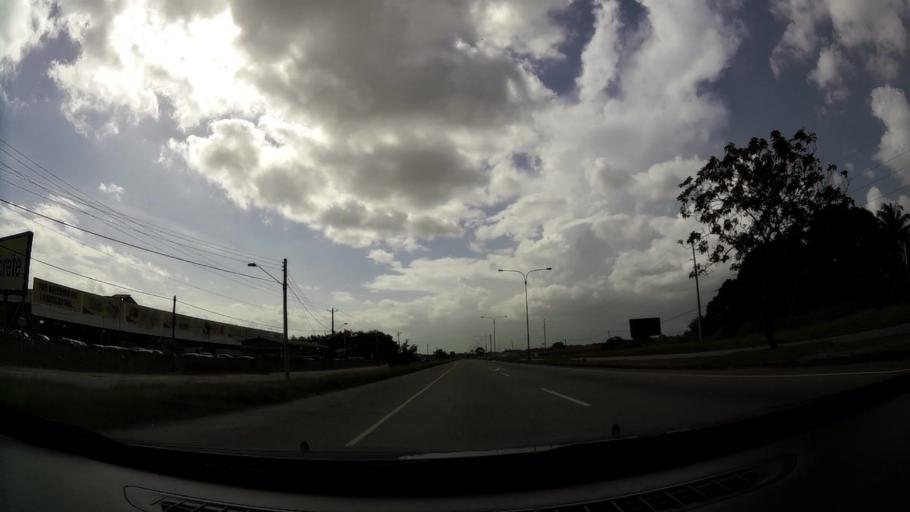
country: TT
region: Tunapuna/Piarco
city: Arouca
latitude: 10.6149
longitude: -61.3274
